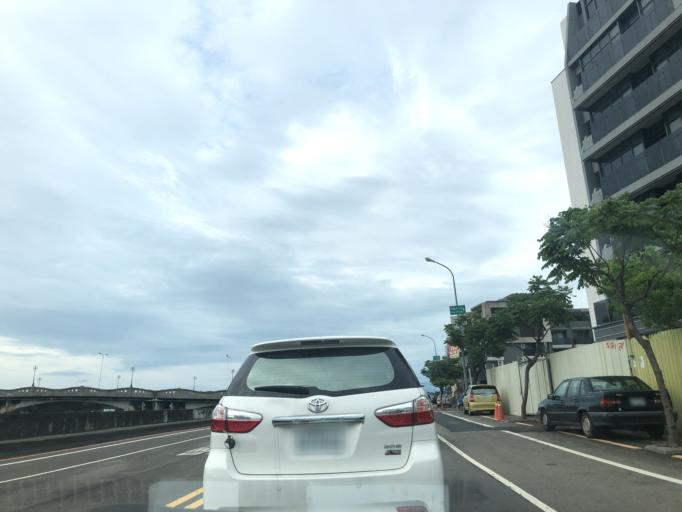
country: TW
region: Taiwan
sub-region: Taichung City
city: Taichung
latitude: 24.1092
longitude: 120.6981
